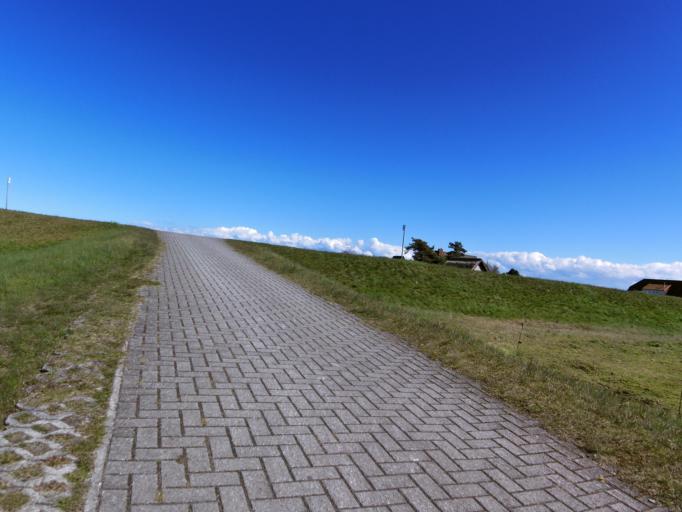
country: DE
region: Mecklenburg-Vorpommern
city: Hiddensee
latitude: 54.5257
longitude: 13.0910
